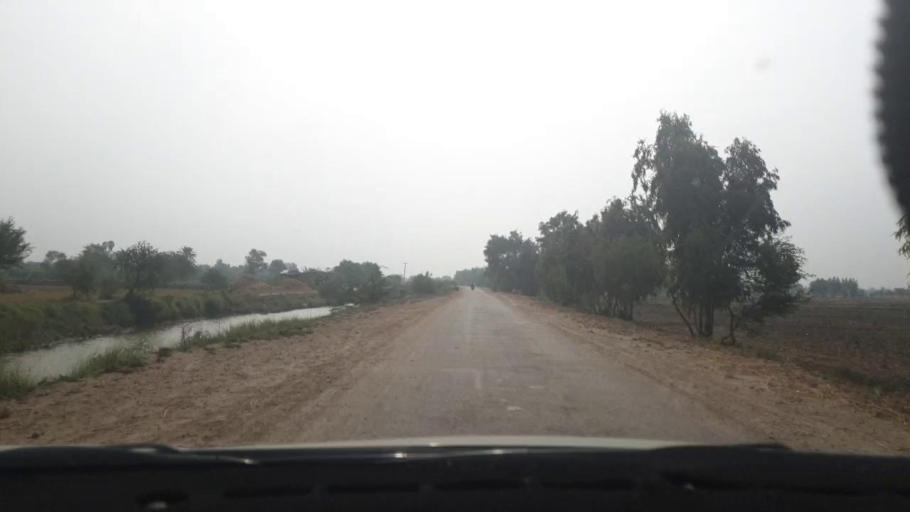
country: PK
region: Sindh
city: Tando Muhammad Khan
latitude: 25.0516
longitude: 68.5505
